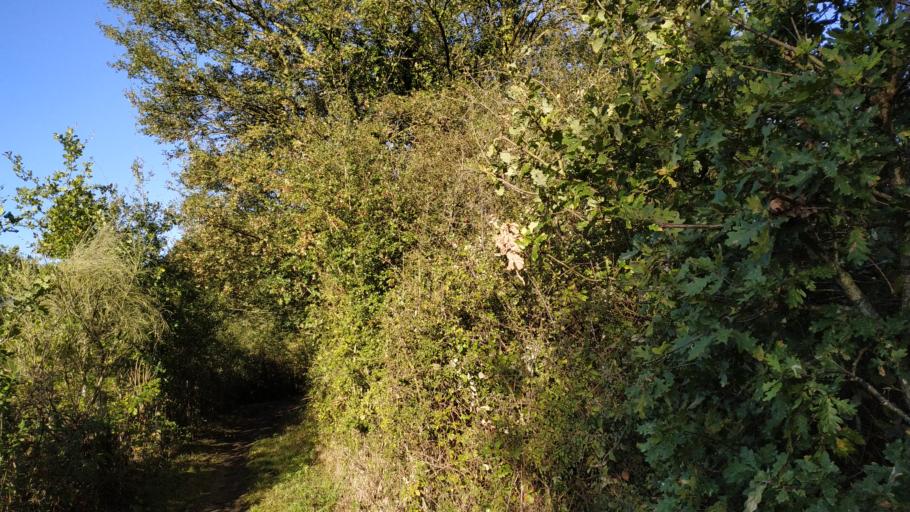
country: FR
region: Brittany
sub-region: Departement d'Ille-et-Vilaine
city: Chantepie
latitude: 48.0788
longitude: -1.6232
